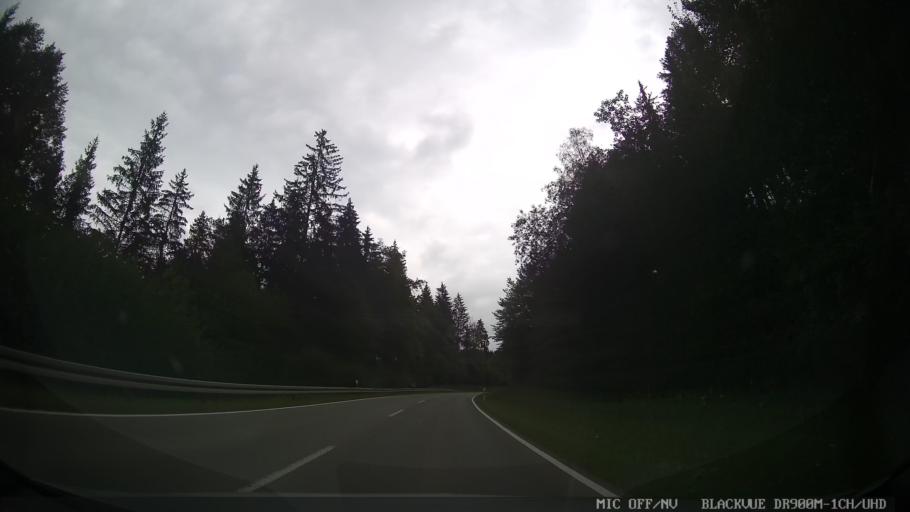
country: DE
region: Baden-Wuerttemberg
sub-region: Freiburg Region
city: Neuhausen ob Eck
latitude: 47.9946
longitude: 8.9319
